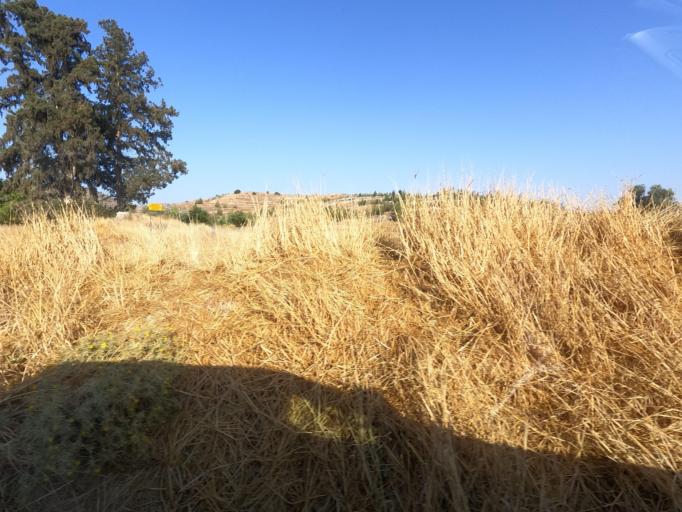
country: CY
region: Lefkosia
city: Lympia
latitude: 34.9916
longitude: 33.4374
